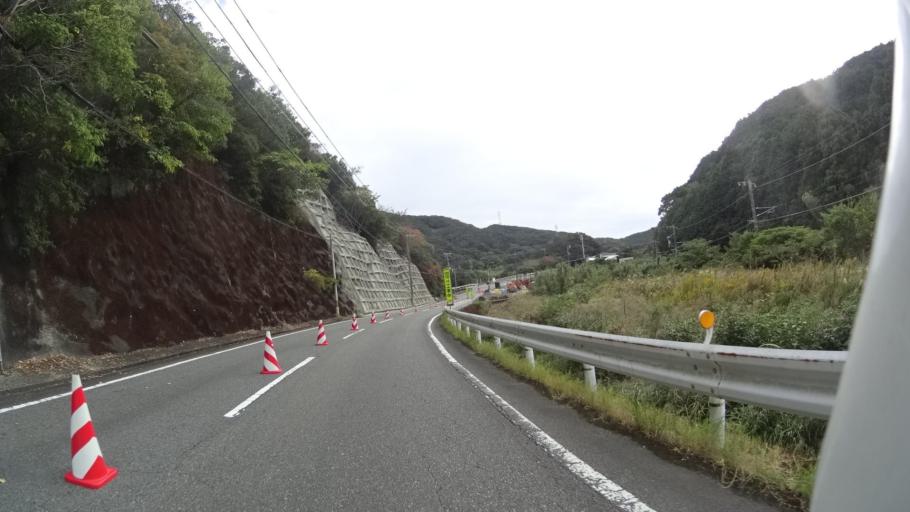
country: JP
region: Wakayama
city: Shingu
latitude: 33.4934
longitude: 135.7595
